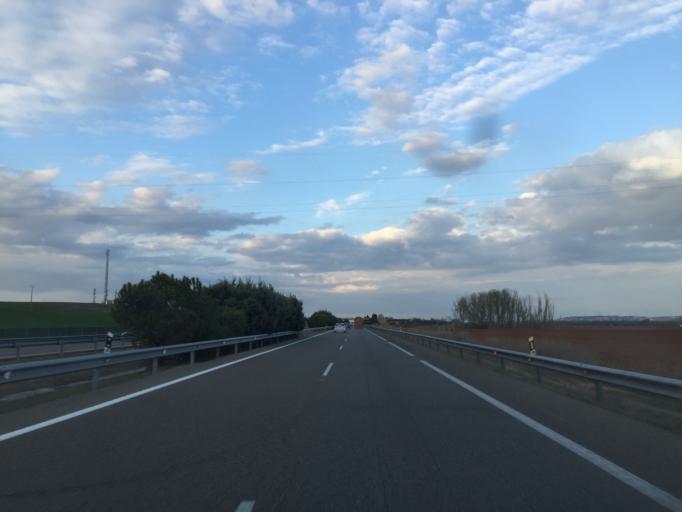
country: ES
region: Castille and Leon
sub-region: Provincia de Palencia
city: Villamediana
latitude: 42.0112
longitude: -4.3542
